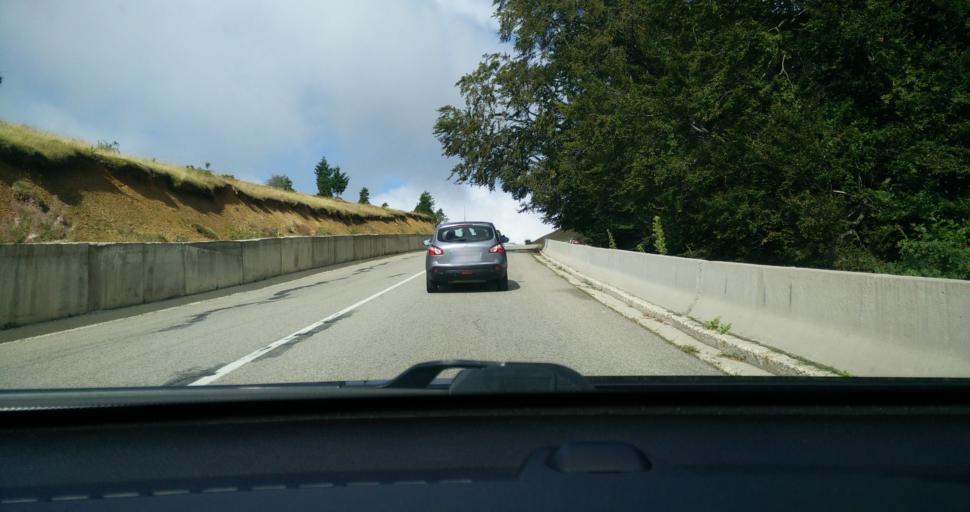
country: RO
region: Gorj
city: Novaci-Straini
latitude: 45.2294
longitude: 23.6914
